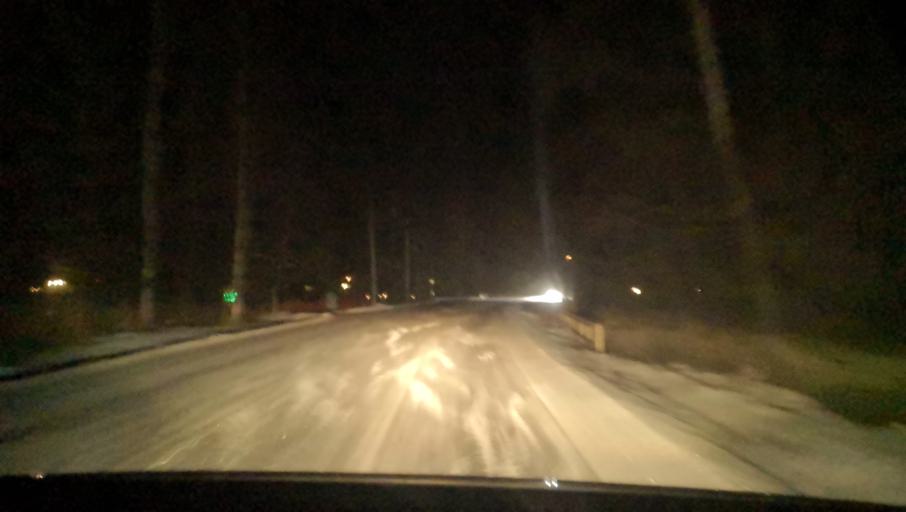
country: SE
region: Uppsala
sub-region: Heby Kommun
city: Tarnsjo
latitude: 60.1407
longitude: 16.9079
